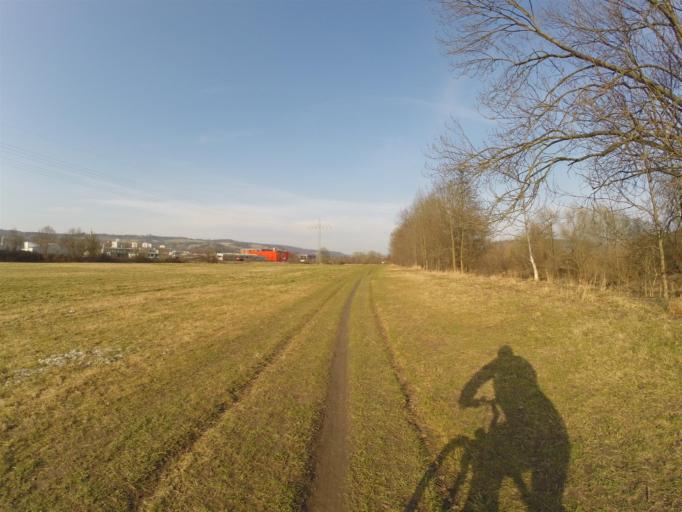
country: DE
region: Thuringia
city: Jena
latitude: 50.9436
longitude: 11.6099
